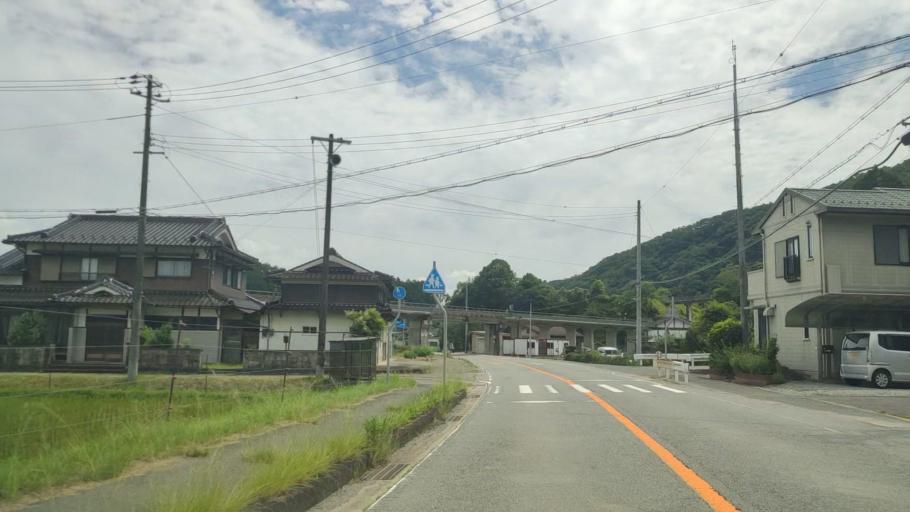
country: JP
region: Hyogo
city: Yamazakicho-nakabirose
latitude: 35.0360
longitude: 134.3675
